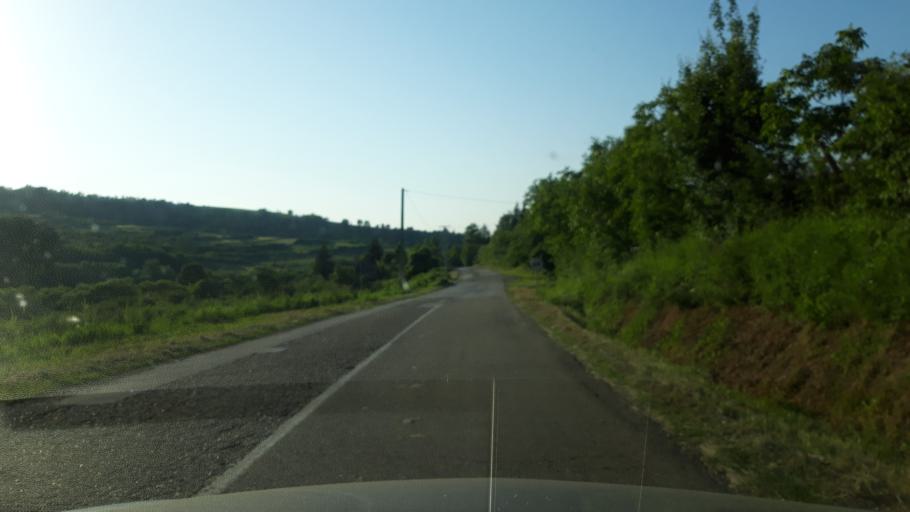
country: RS
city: Glozan
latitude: 45.1621
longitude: 19.5902
